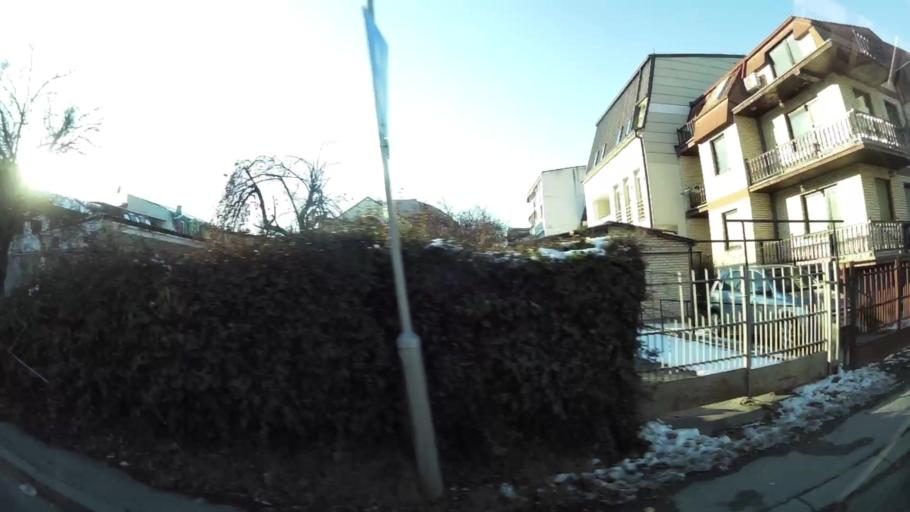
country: MK
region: Karpos
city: Skopje
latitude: 41.9945
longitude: 21.4031
